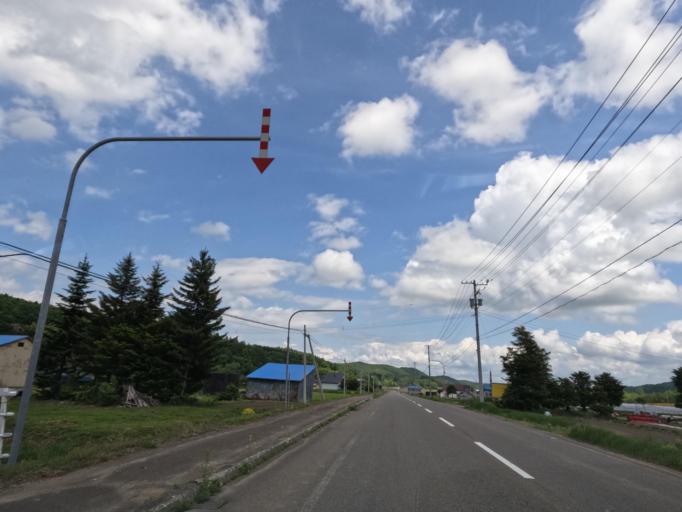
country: JP
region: Hokkaido
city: Takikawa
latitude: 43.5861
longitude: 141.7726
